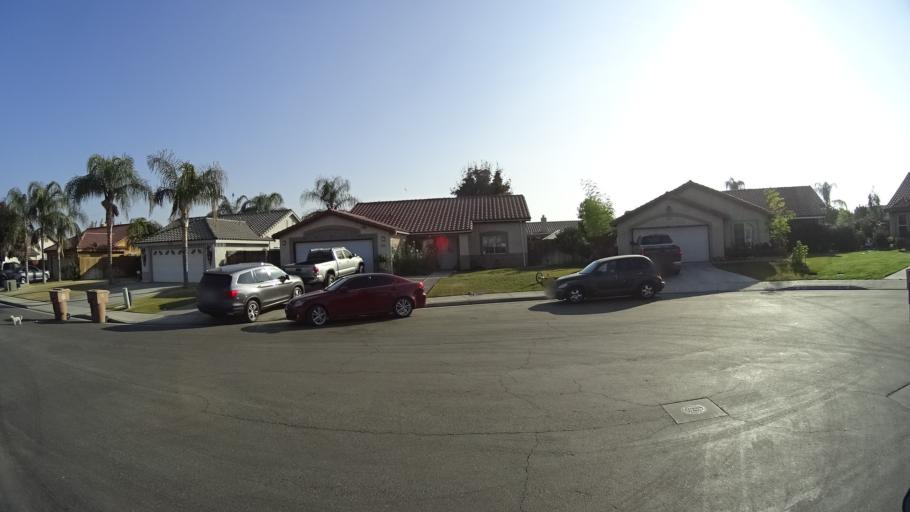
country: US
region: California
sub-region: Kern County
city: Greenfield
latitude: 35.2894
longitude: -119.0135
